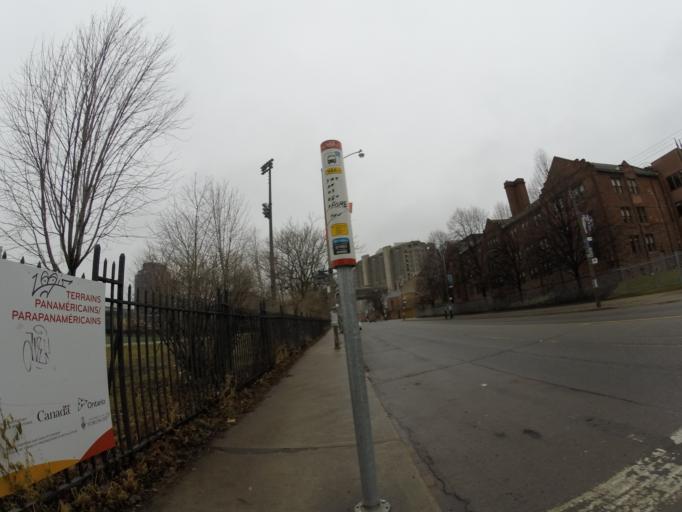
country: CA
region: Ontario
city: Toronto
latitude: 43.6646
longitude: -79.3959
